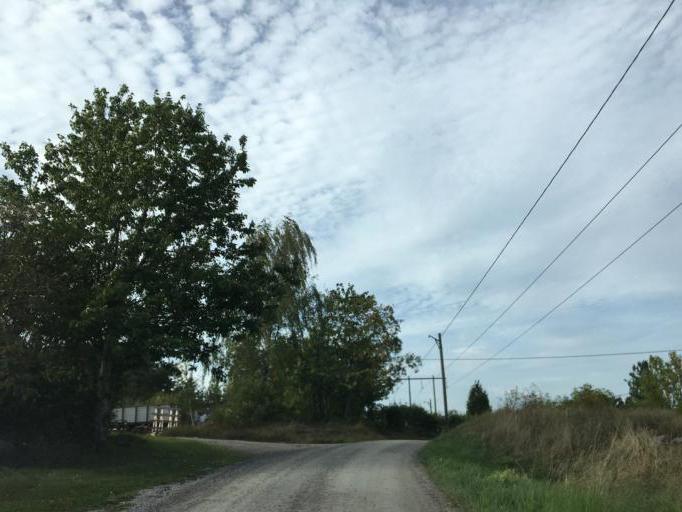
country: SE
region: Soedermanland
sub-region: Eskilstuna Kommun
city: Eskilstuna
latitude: 59.4030
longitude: 16.5075
